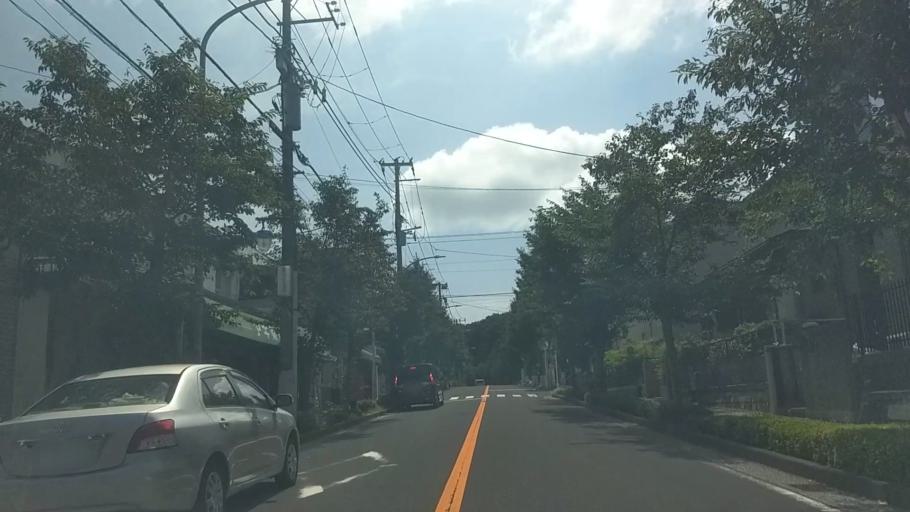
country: JP
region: Kanagawa
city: Yokosuka
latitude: 35.3475
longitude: 139.6284
